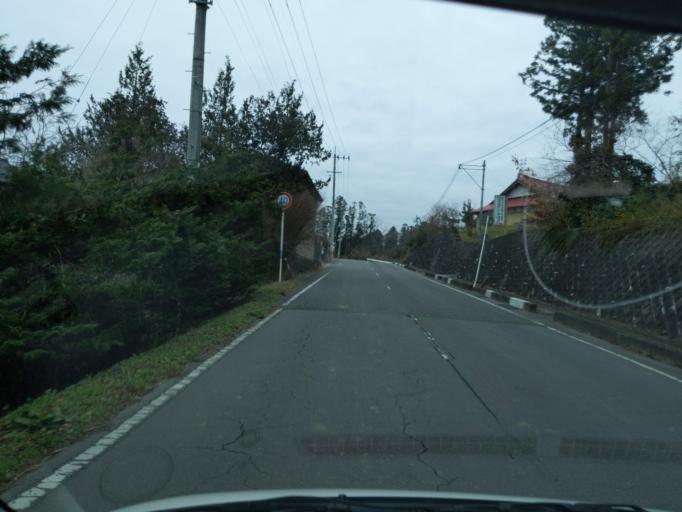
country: JP
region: Iwate
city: Ichinoseki
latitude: 38.7381
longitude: 141.2489
